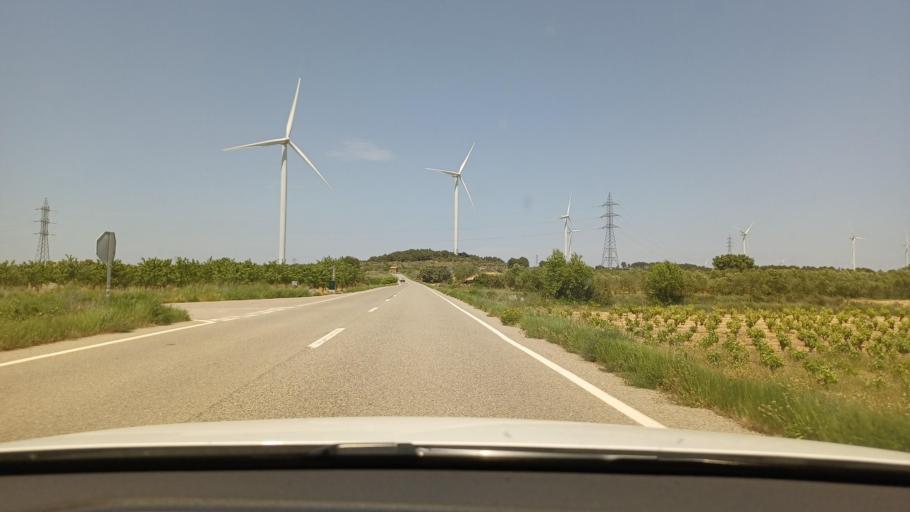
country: ES
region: Catalonia
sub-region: Provincia de Tarragona
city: Vilalba dels Arcs
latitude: 41.0966
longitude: 0.4181
